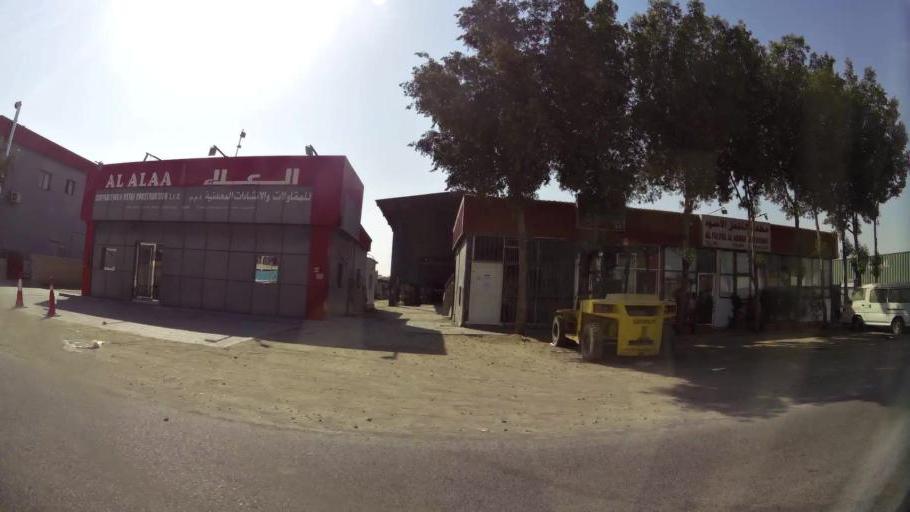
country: AE
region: Ajman
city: Ajman
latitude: 25.4350
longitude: 55.5160
